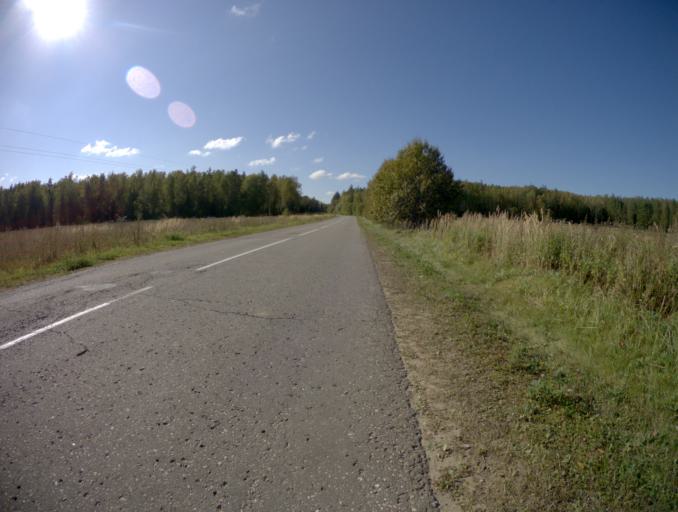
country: RU
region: Vladimir
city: Kameshkovo
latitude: 56.3536
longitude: 40.8634
